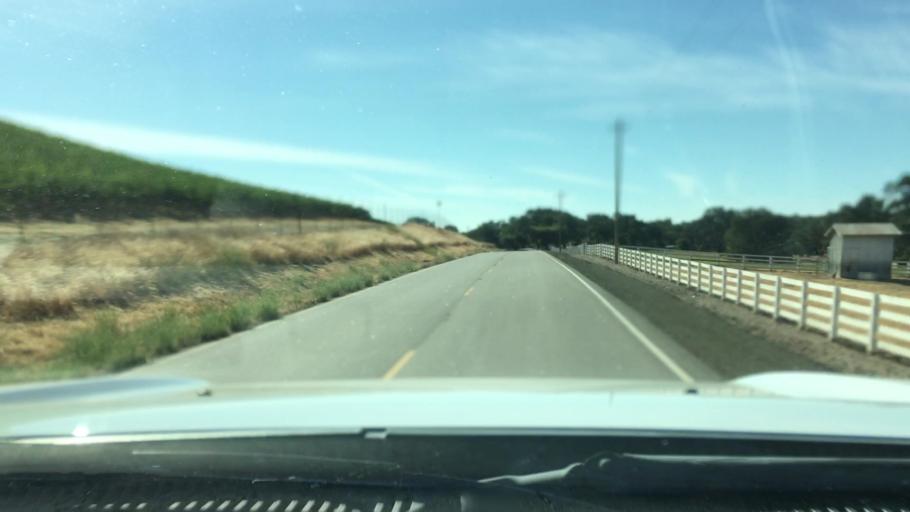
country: US
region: California
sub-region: San Luis Obispo County
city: Templeton
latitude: 35.5574
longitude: -120.6289
